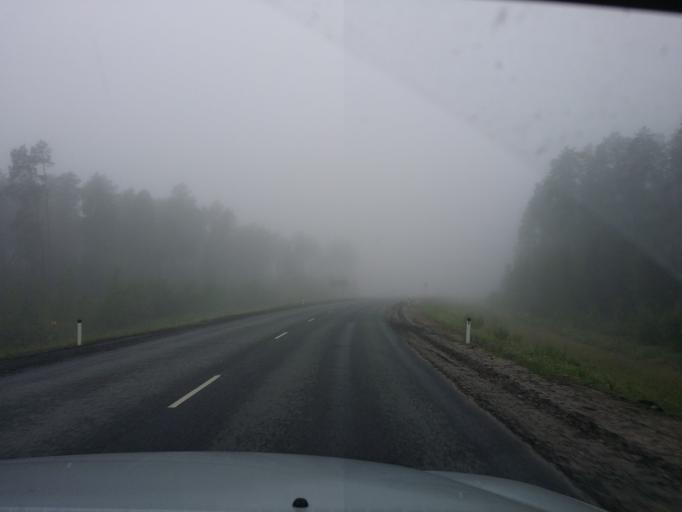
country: RU
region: Khanty-Mansiyskiy Avtonomnyy Okrug
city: Gornopravdinsk
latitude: 59.6908
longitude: 70.1098
